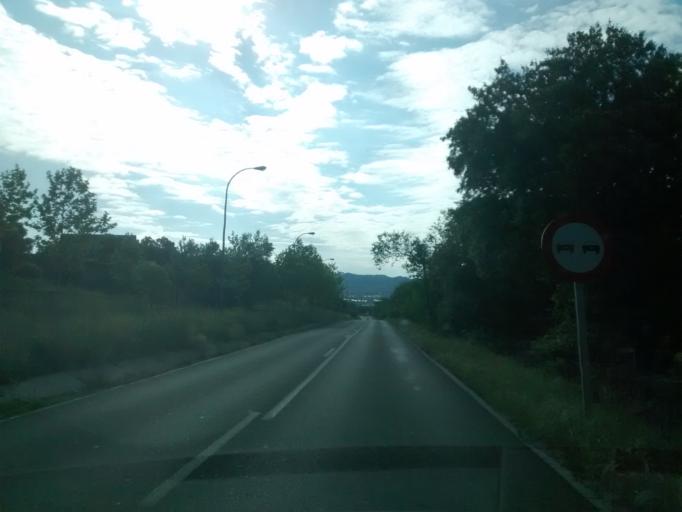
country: ES
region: Madrid
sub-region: Provincia de Madrid
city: Alpedrete
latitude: 40.6525
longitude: -4.0153
